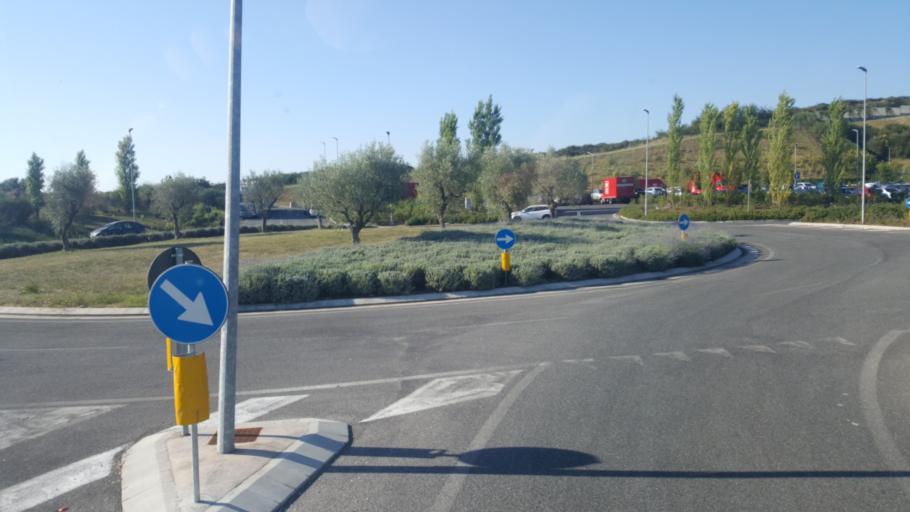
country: IT
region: Latium
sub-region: Citta metropolitana di Roma Capitale
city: Albuccione
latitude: 41.9692
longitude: 12.6893
